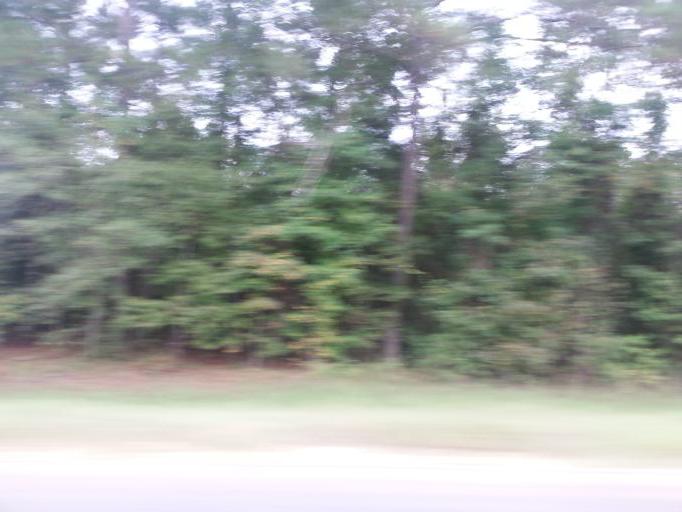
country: US
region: Alabama
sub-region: Butler County
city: Georgiana
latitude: 31.6045
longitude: -86.8220
